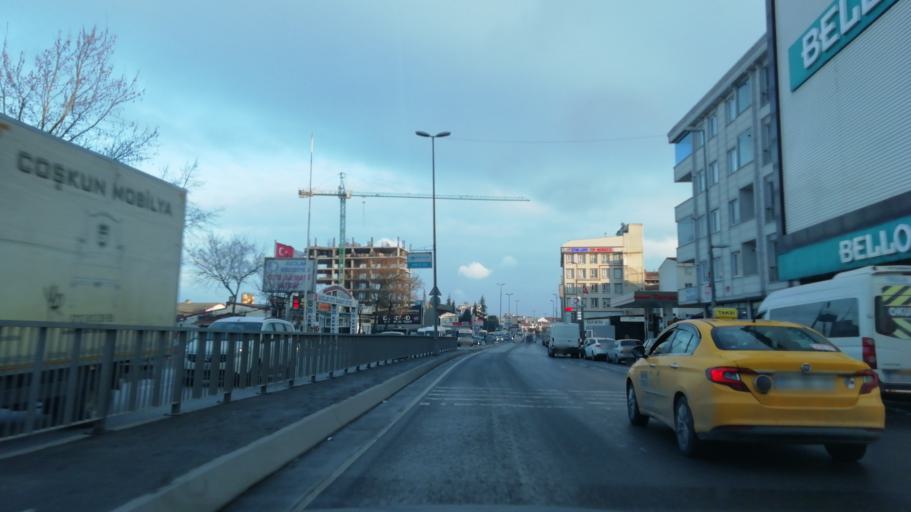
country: TR
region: Istanbul
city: Esenyurt
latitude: 41.0122
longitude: 28.6974
